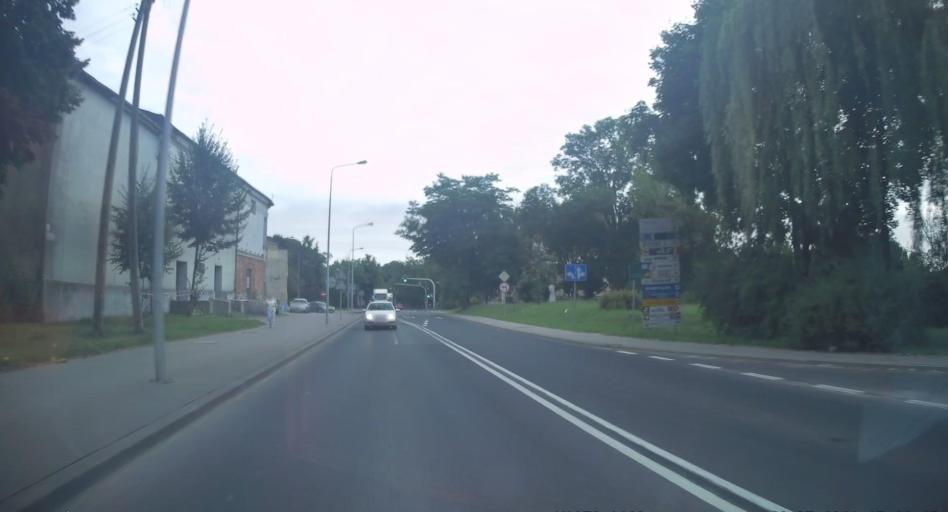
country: PL
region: Lodz Voivodeship
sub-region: Powiat radomszczanski
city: Radomsko
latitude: 51.0711
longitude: 19.4459
